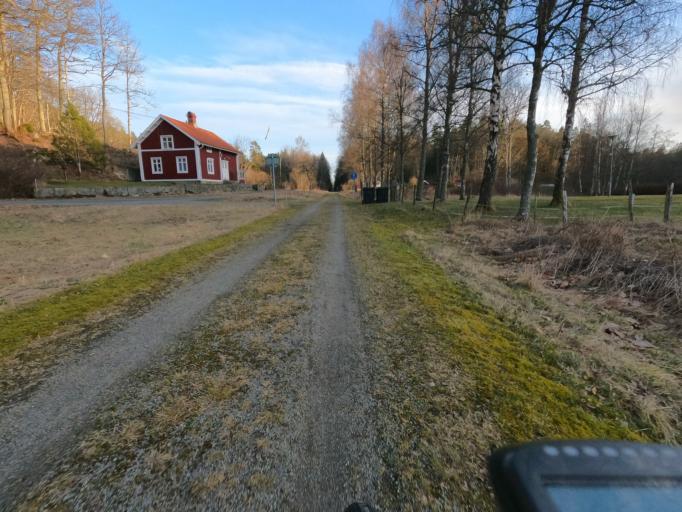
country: SE
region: Blekinge
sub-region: Karlshamns Kommun
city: Svangsta
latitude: 56.3669
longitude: 14.6857
